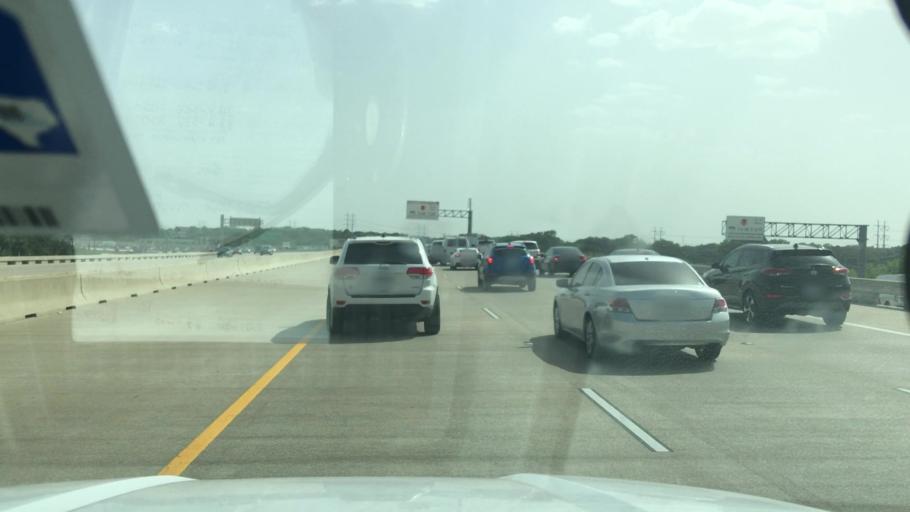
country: US
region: Texas
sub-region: Dallas County
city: Grand Prairie
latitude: 32.7806
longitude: -97.0247
